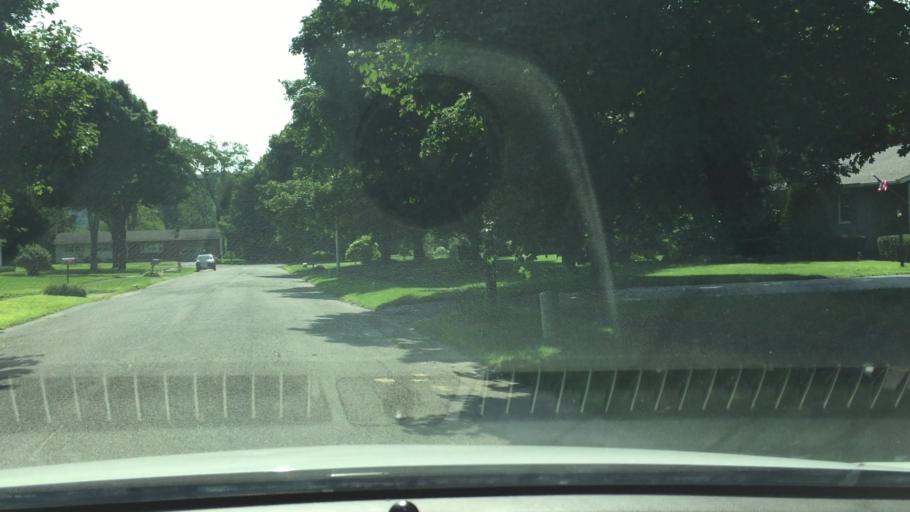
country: US
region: Massachusetts
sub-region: Berkshire County
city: Pittsfield
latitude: 42.4170
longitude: -73.2441
